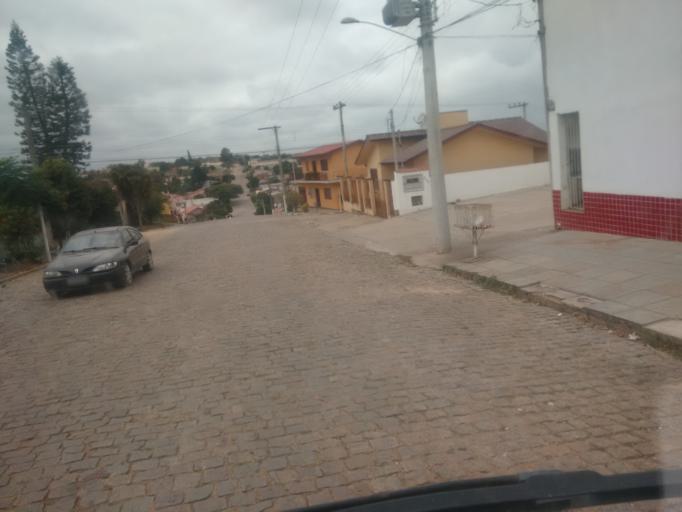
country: BR
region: Rio Grande do Sul
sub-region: Camaqua
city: Camaqua
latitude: -30.8378
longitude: -51.8178
